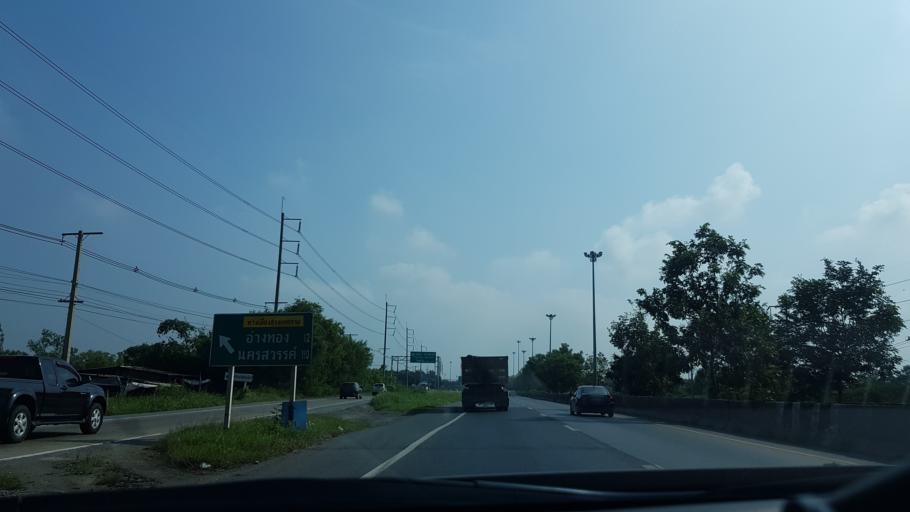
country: TH
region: Phra Nakhon Si Ayutthaya
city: Bang Pa-in
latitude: 14.1537
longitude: 100.5621
